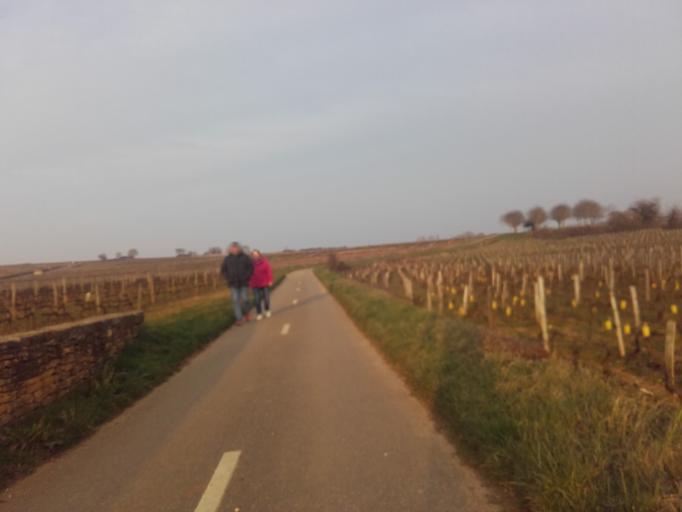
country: FR
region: Bourgogne
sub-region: Departement de Saone-et-Loire
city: Chagny
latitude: 46.9145
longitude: 4.7118
